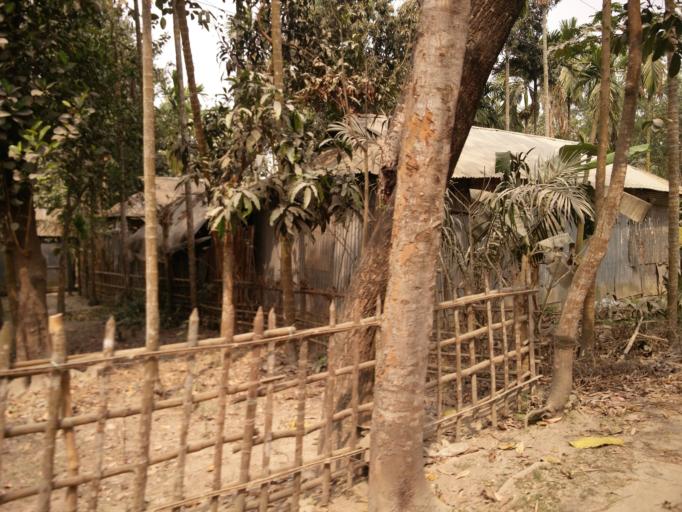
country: BD
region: Rangpur Division
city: Nageswari
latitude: 25.8869
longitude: 89.7049
